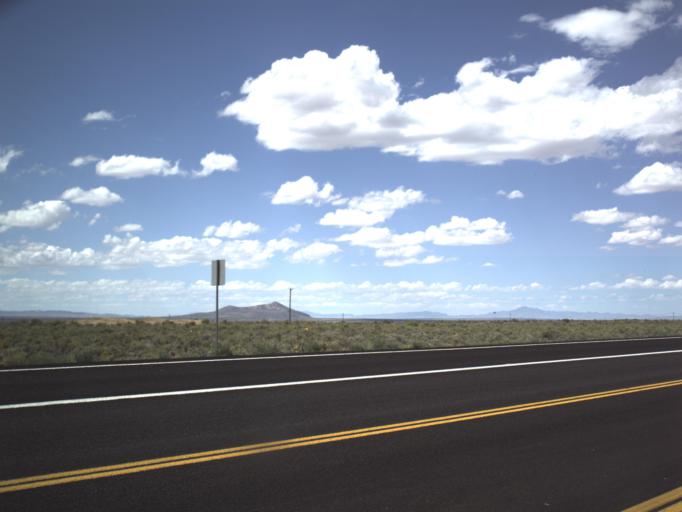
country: US
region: Utah
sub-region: Millard County
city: Fillmore
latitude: 39.1185
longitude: -112.3537
